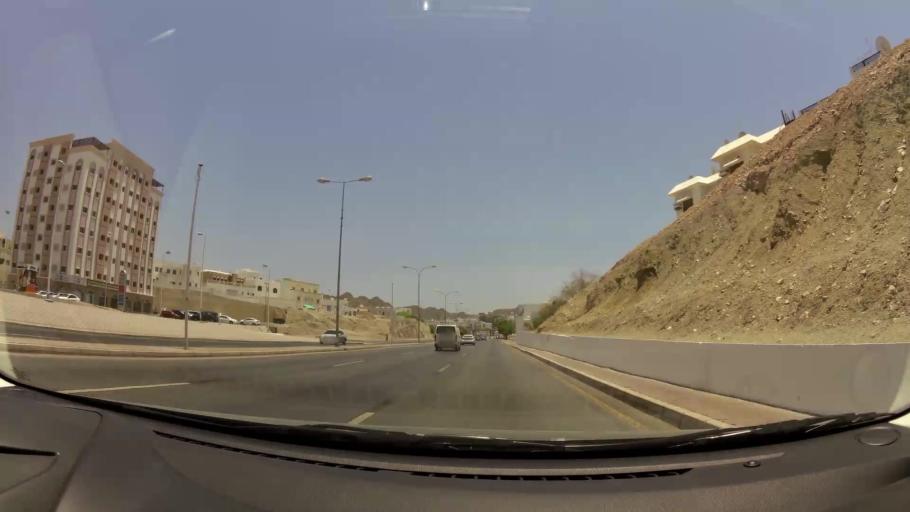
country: OM
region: Muhafazat Masqat
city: Muscat
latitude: 23.6112
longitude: 58.5410
